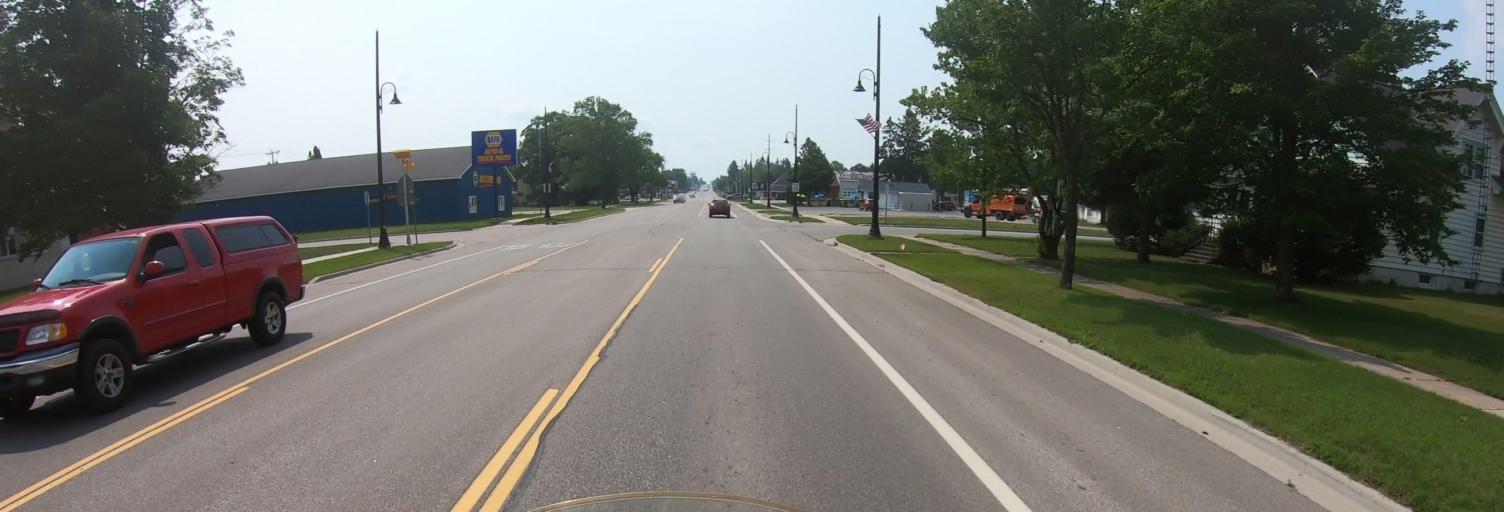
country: US
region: Michigan
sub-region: Luce County
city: Newberry
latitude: 46.3491
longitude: -85.5099
